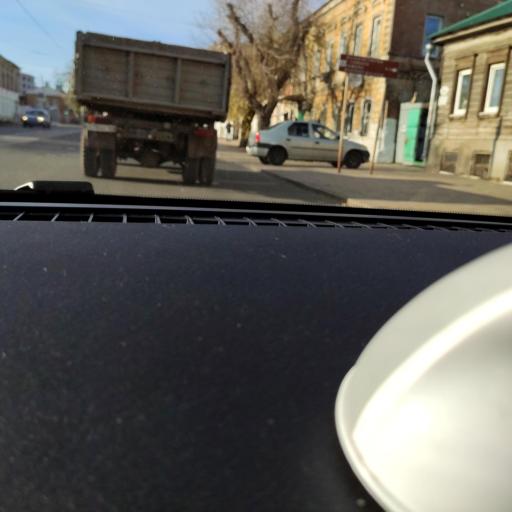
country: RU
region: Samara
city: Rozhdestveno
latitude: 53.1823
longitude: 50.0897
